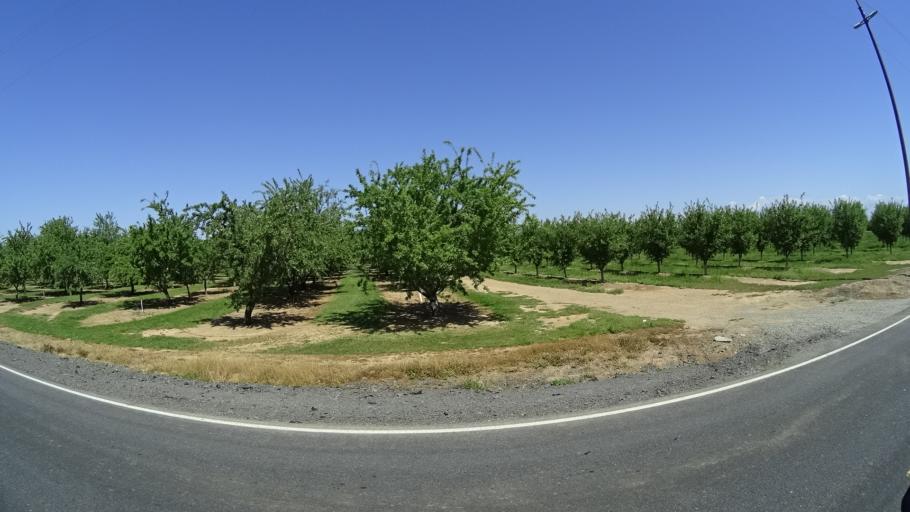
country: US
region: California
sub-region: Glenn County
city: Hamilton City
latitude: 39.7673
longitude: -122.0997
